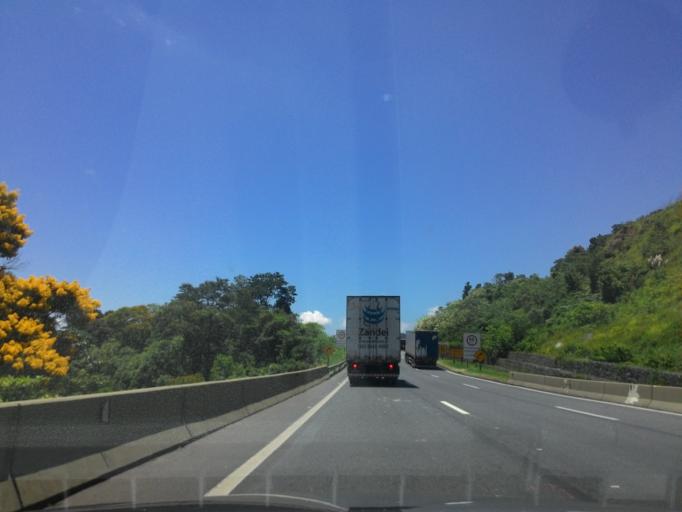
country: BR
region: Sao Paulo
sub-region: Cajati
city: Cajati
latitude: -24.9683
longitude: -48.4831
